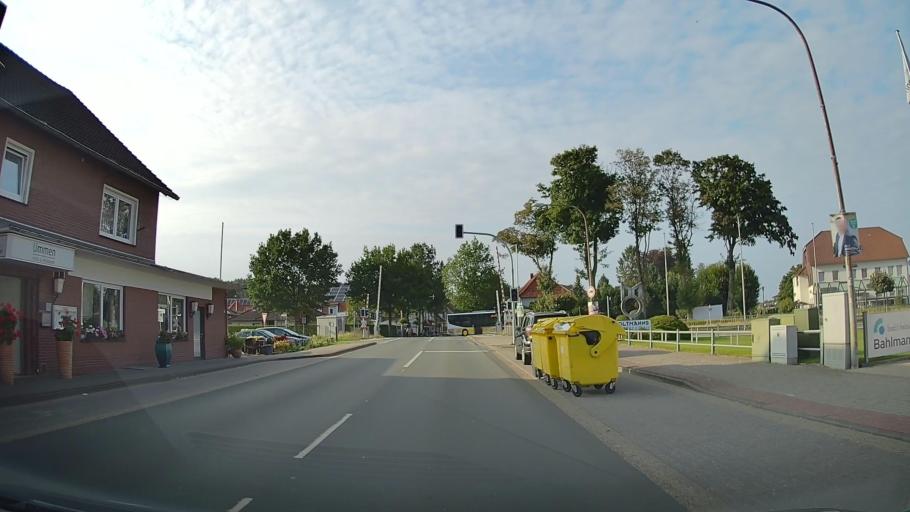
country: DE
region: Lower Saxony
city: Barssel
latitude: 53.1654
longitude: 7.7478
